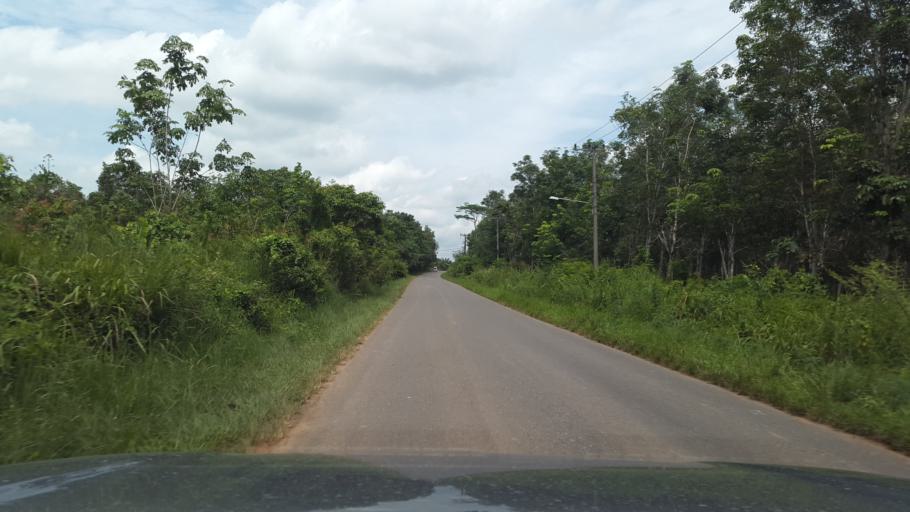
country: ID
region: South Sumatra
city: Gunungmegang Dalam
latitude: -3.3461
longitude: 103.9164
